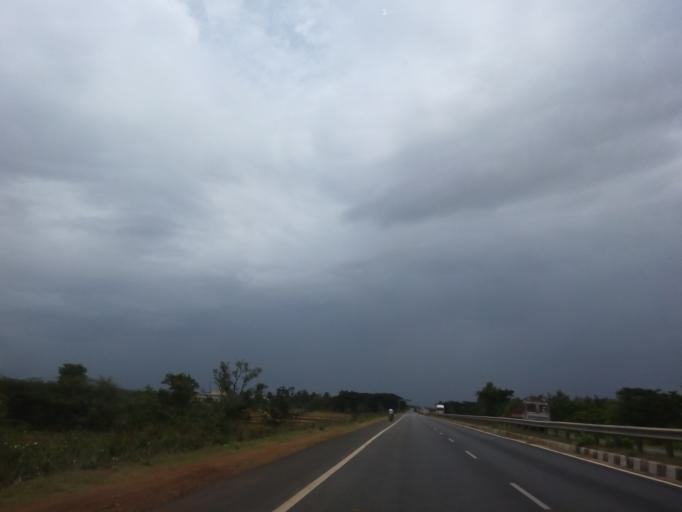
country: IN
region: Karnataka
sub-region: Davanagere
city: Harihar
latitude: 14.4726
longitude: 75.8290
